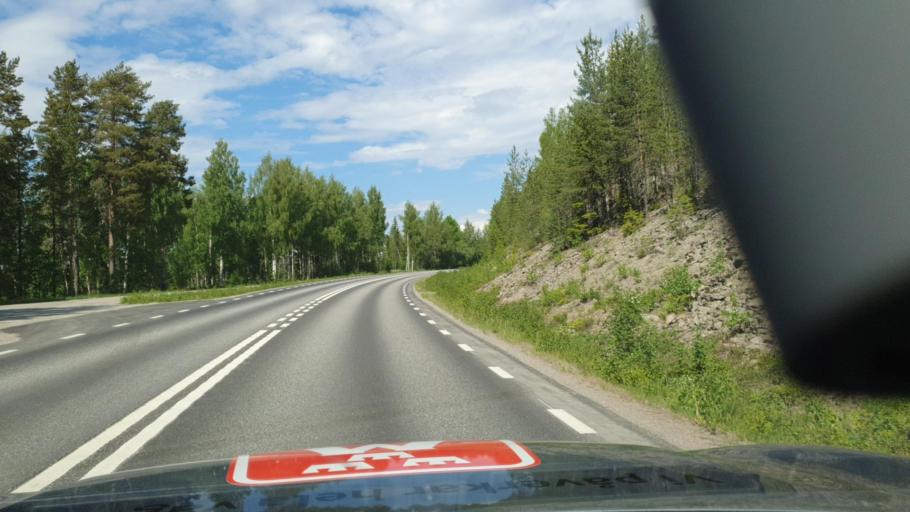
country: SE
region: Vaesternorrland
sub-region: Solleftea Kommun
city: As
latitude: 63.6616
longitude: 16.7860
